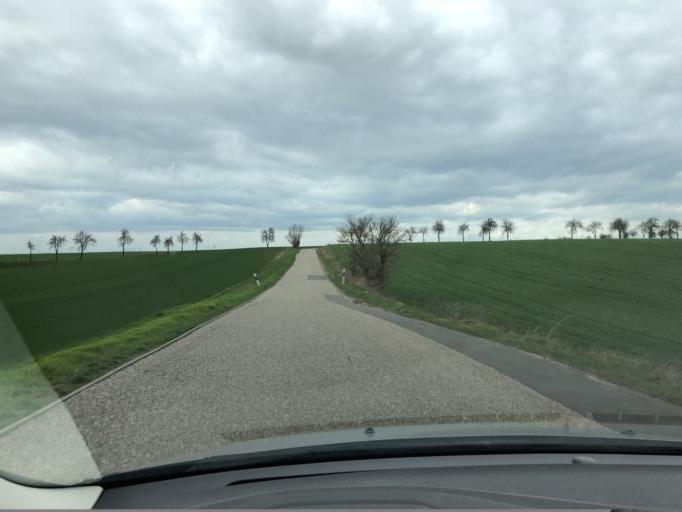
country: DE
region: Saxony-Anhalt
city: Muschwitz
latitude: 51.1964
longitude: 12.1328
